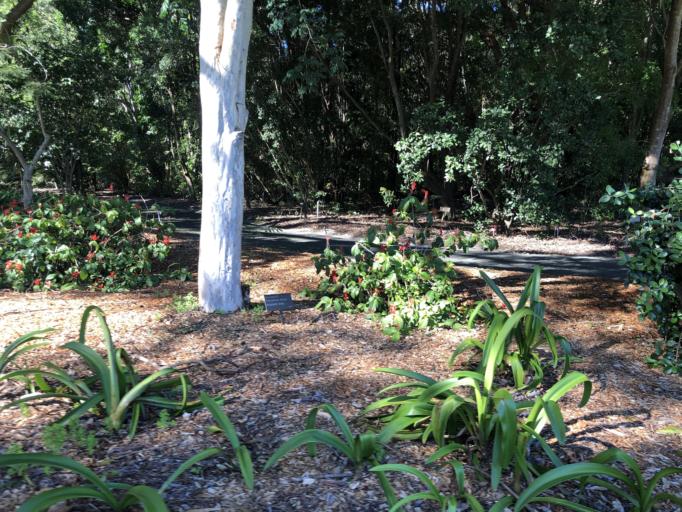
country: AU
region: New South Wales
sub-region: Coffs Harbour
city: Coffs Harbour
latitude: -30.2932
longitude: 153.1256
